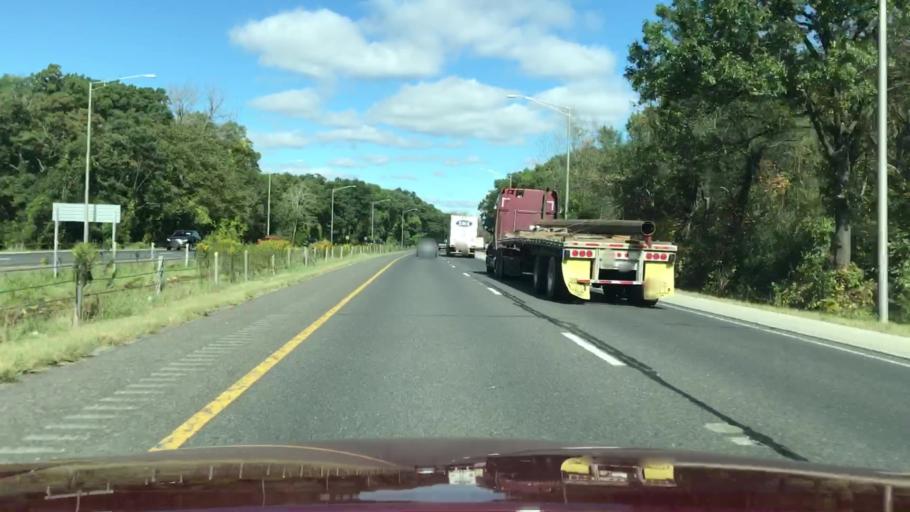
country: US
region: Illinois
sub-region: Cook County
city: Glenwood
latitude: 41.5504
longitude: -87.5831
